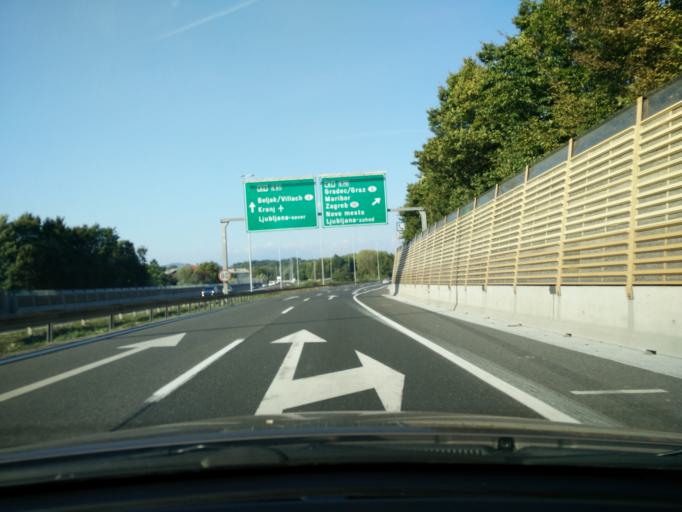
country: SI
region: Brezovica
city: Vnanje Gorice
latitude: 46.0333
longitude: 14.4472
